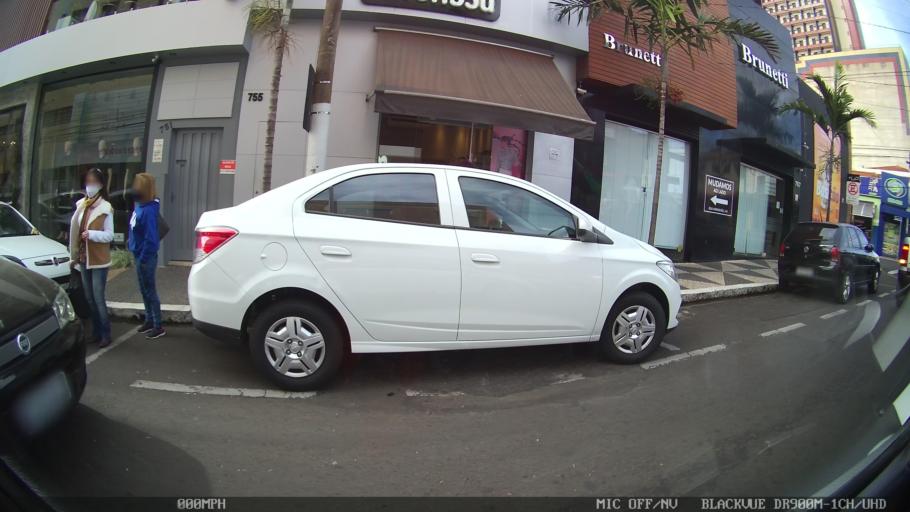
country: BR
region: Sao Paulo
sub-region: Catanduva
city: Catanduva
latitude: -21.1372
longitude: -48.9739
